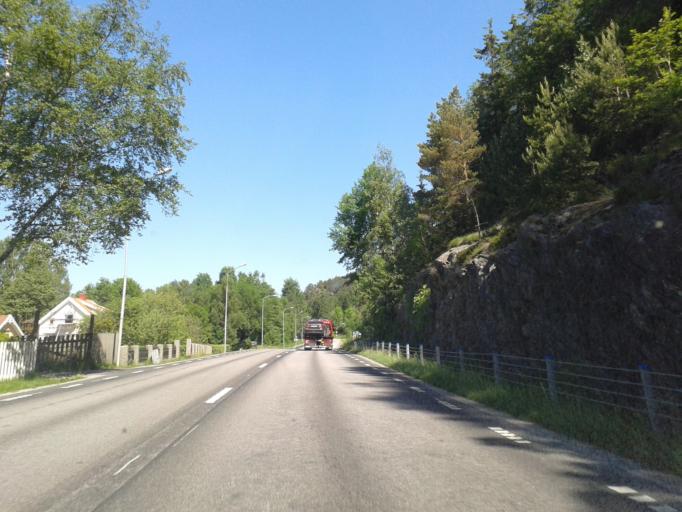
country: SE
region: Vaestra Goetaland
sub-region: Orust
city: Henan
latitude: 58.2267
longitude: 11.6855
